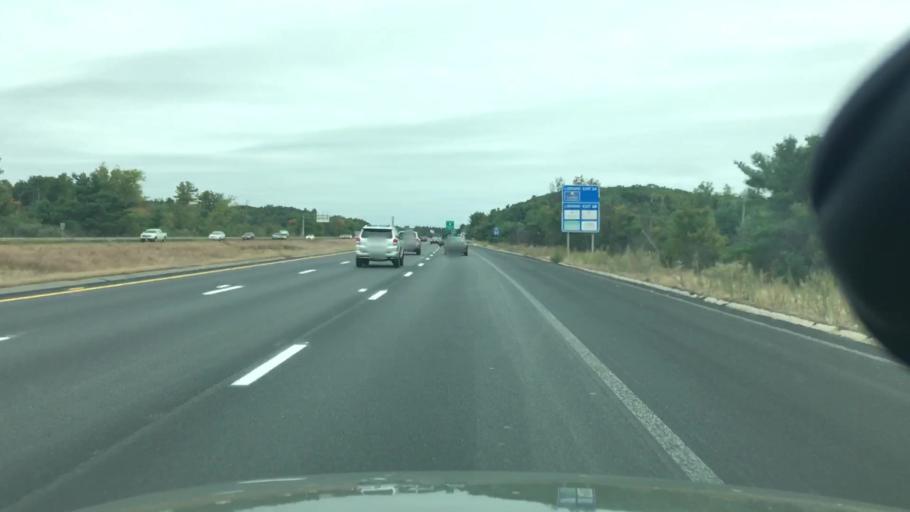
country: US
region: Massachusetts
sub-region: Worcester County
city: Sturbridge
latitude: 42.0979
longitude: -72.0860
